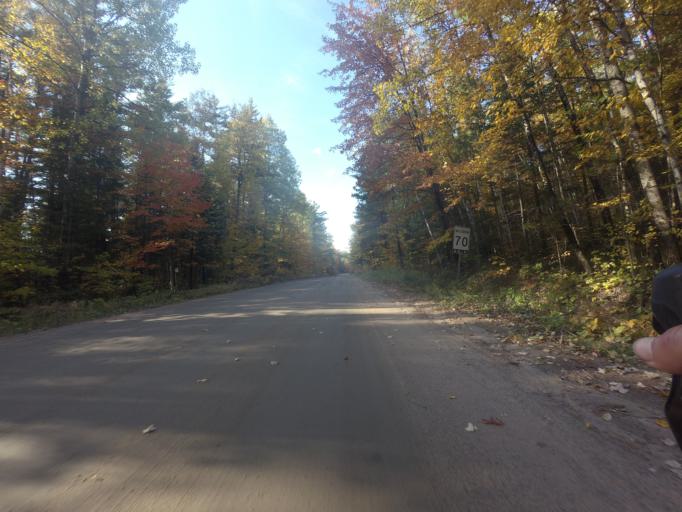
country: CA
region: Ontario
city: Deep River
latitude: 45.8764
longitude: -77.5654
